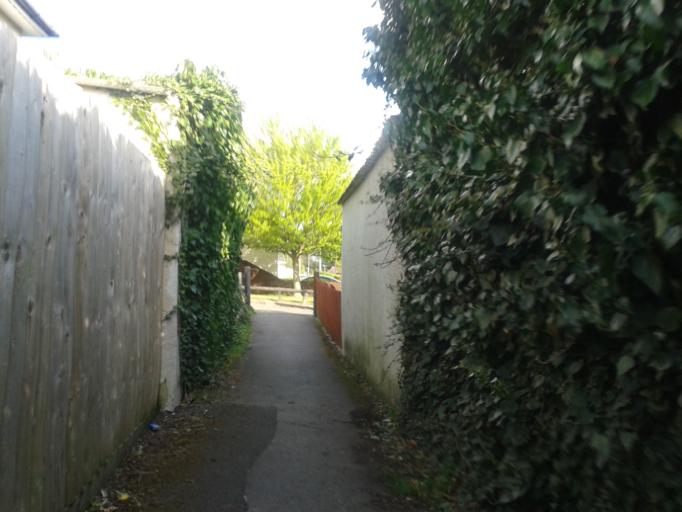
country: GB
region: England
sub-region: Cambridgeshire
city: Cambridge
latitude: 52.1886
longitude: 0.1589
